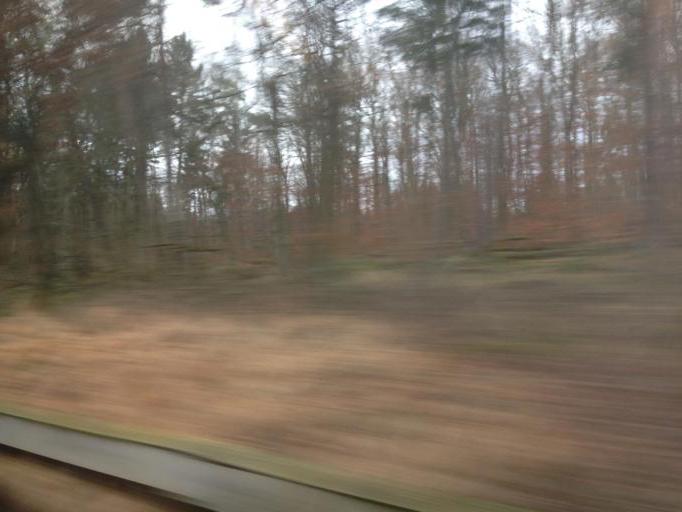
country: DE
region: Hesse
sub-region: Regierungsbezirk Giessen
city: Giessen
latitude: 50.5516
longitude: 8.7093
